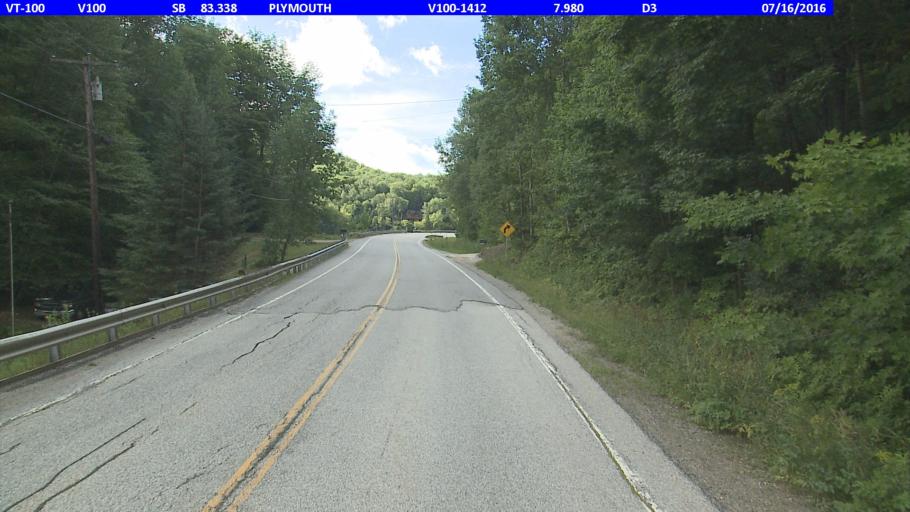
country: US
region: Vermont
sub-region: Rutland County
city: Rutland
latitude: 43.5636
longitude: -72.7605
